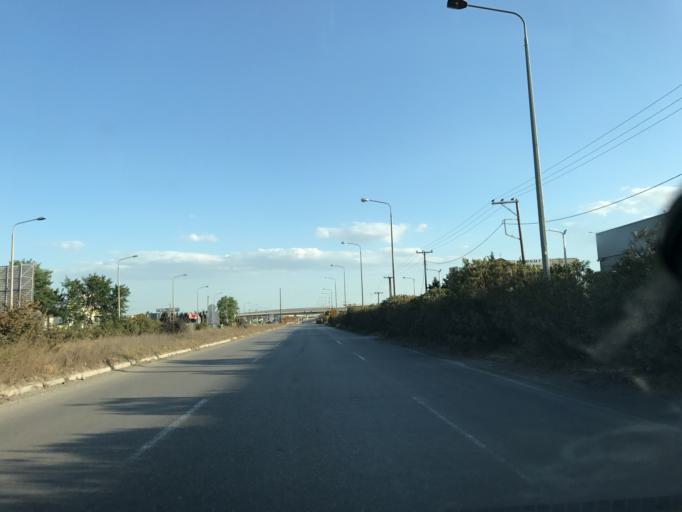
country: GR
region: Central Macedonia
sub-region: Nomos Thessalonikis
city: Menemeni
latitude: 40.6611
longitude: 22.8816
